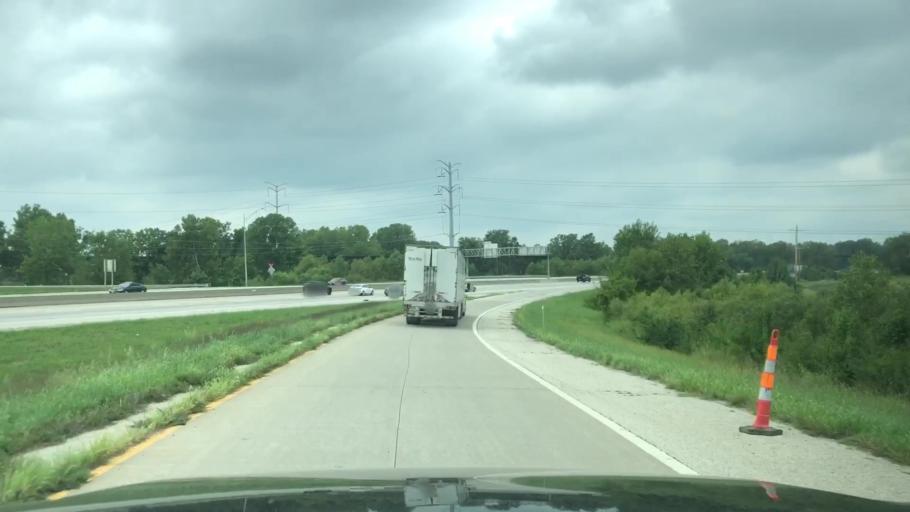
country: US
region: Missouri
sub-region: Saint Charles County
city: Saint Charles
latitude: 38.7928
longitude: -90.4542
